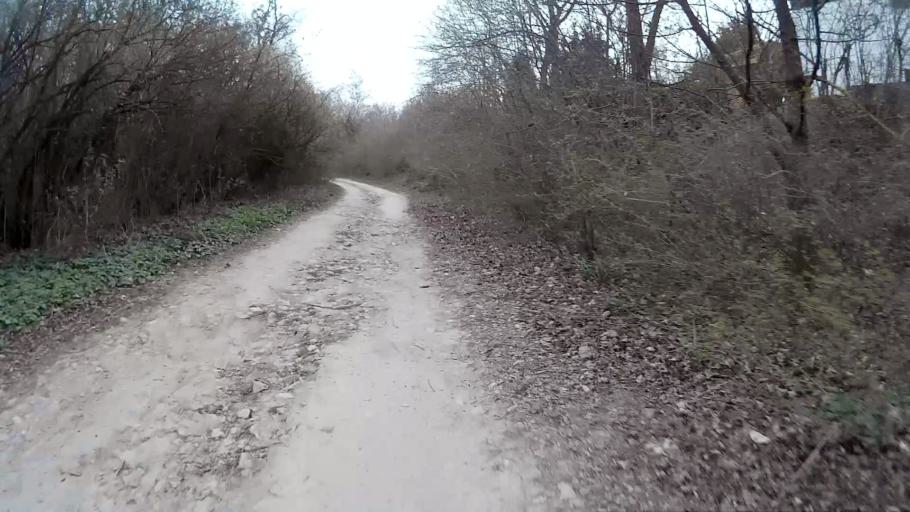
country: CZ
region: South Moravian
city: Ivancice
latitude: 49.0894
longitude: 16.3509
